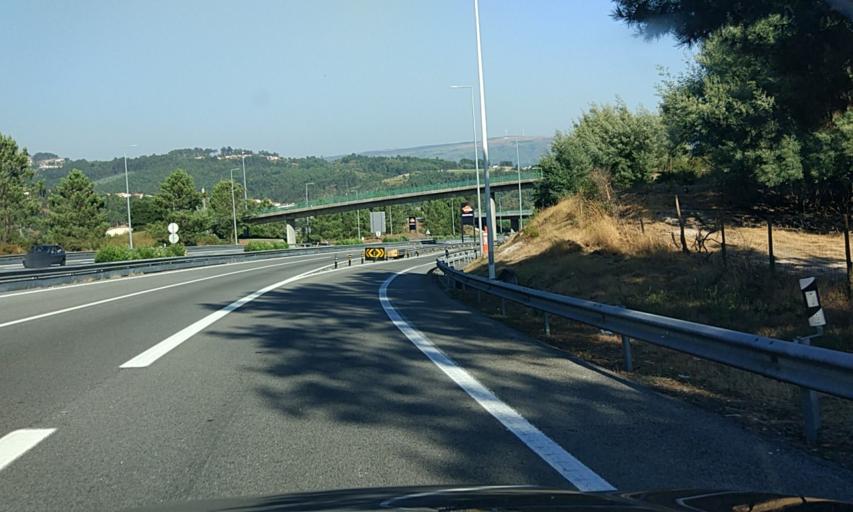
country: PT
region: Porto
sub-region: Marco de Canaveses
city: Marco de Canavezes
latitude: 41.2346
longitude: -8.1842
